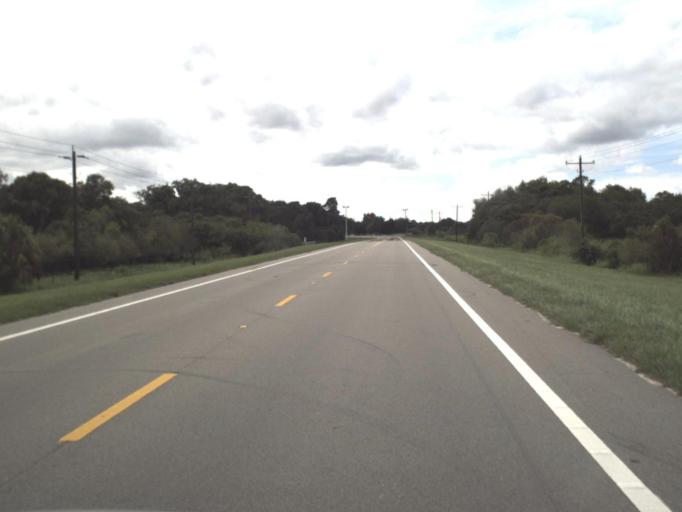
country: US
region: Florida
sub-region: Hillsborough County
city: Sun City Center
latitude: 27.5933
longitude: -82.3792
